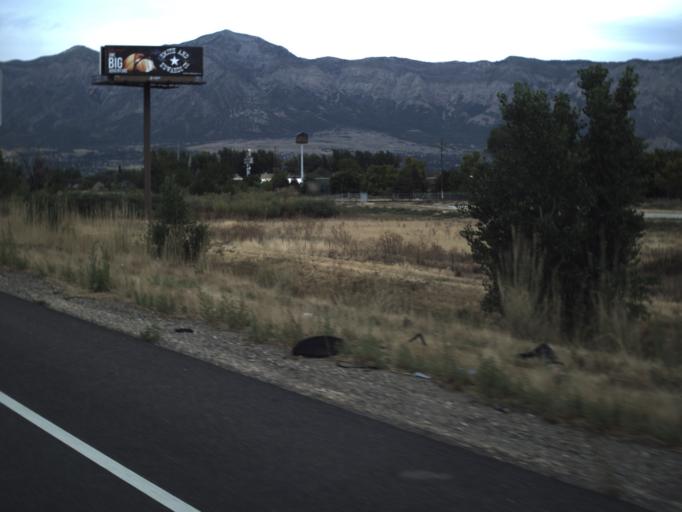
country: US
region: Utah
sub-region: Weber County
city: Marriott-Slaterville
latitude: 41.2399
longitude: -112.0146
